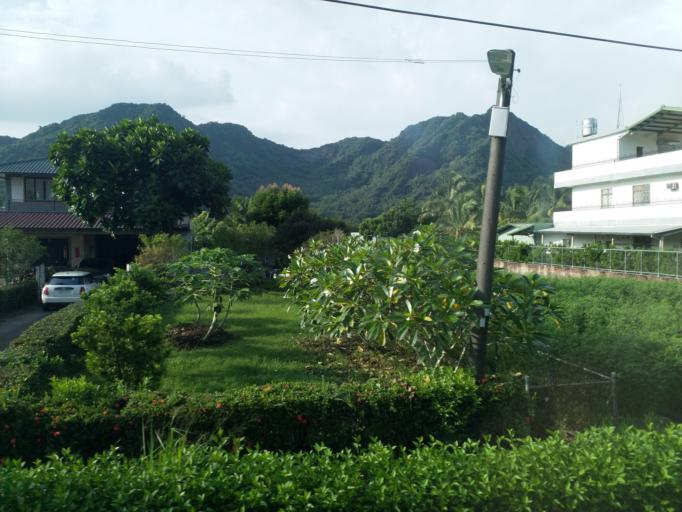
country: TW
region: Taiwan
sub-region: Pingtung
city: Pingtung
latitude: 22.8927
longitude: 120.5115
